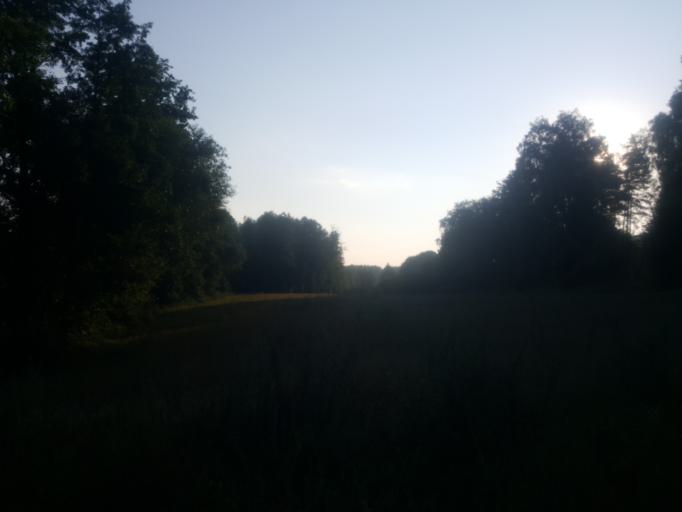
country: LT
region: Alytaus apskritis
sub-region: Alytus
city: Alytus
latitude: 54.3059
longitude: 24.0193
